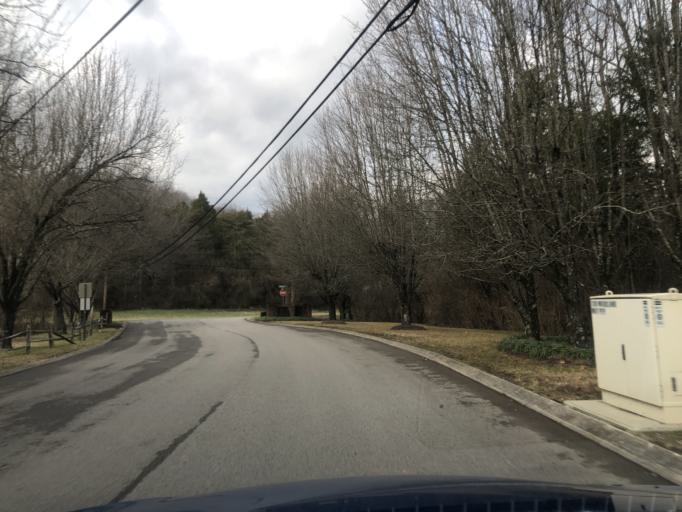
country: US
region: Tennessee
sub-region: Davidson County
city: Belle Meade
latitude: 36.1081
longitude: -86.9344
